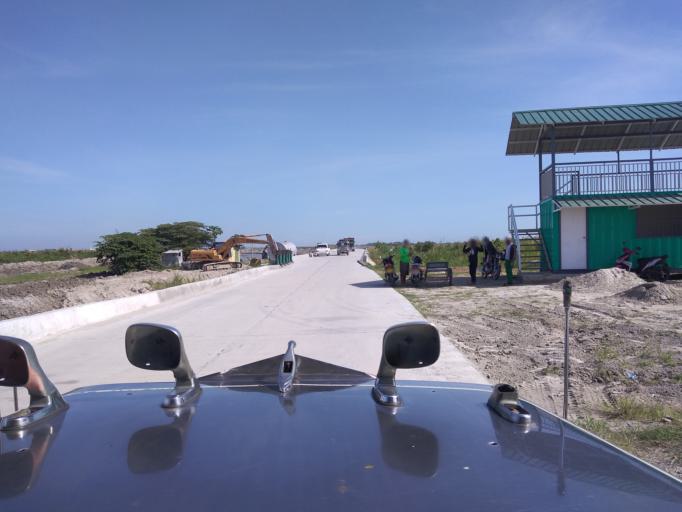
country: PH
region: Central Luzon
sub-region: Province of Pampanga
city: Minalin
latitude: 14.9801
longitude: 120.6835
